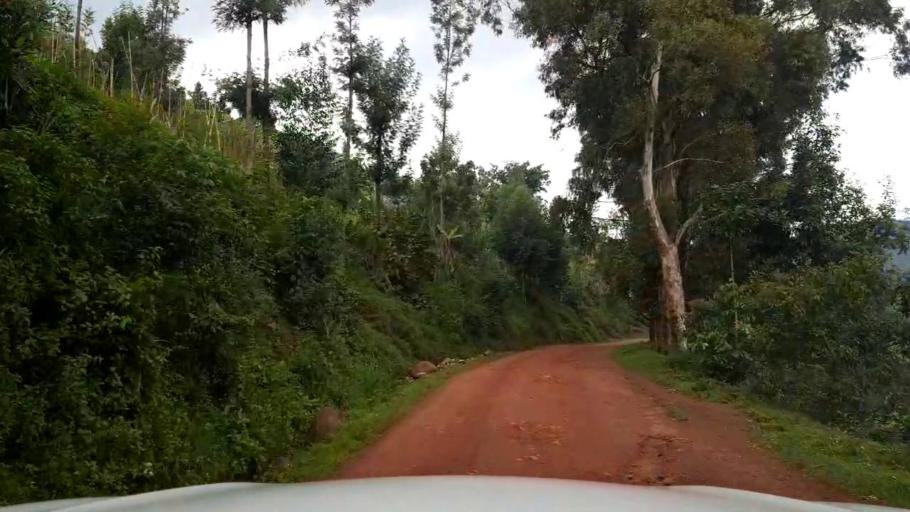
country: UG
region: Western Region
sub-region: Kisoro District
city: Kisoro
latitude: -1.3902
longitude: 29.7976
